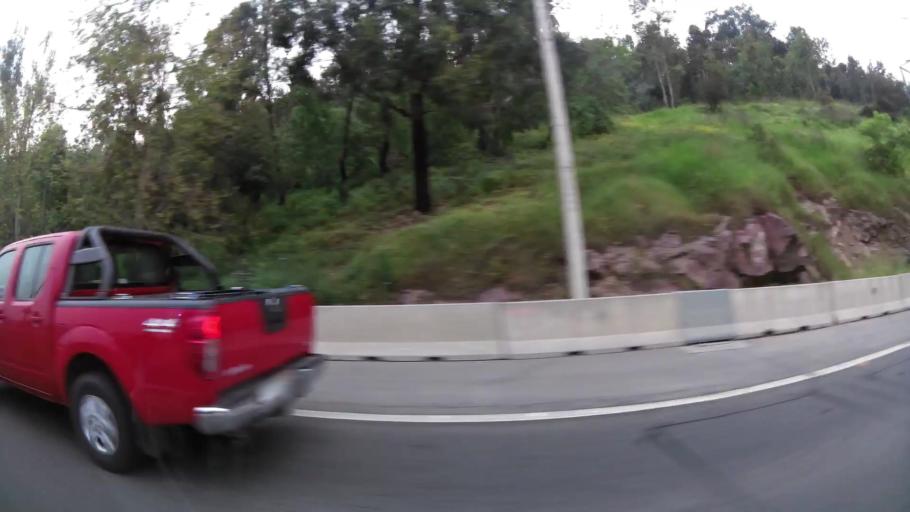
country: CL
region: Santiago Metropolitan
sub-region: Provincia de Santiago
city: Villa Presidente Frei, Nunoa, Santiago, Chile
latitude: -33.3953
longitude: -70.6040
